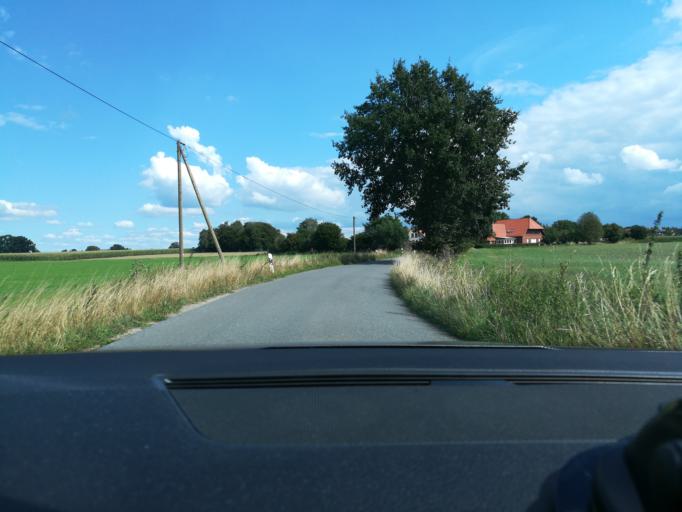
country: DE
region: North Rhine-Westphalia
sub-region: Regierungsbezirk Detmold
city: Hille
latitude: 52.3361
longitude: 8.7154
